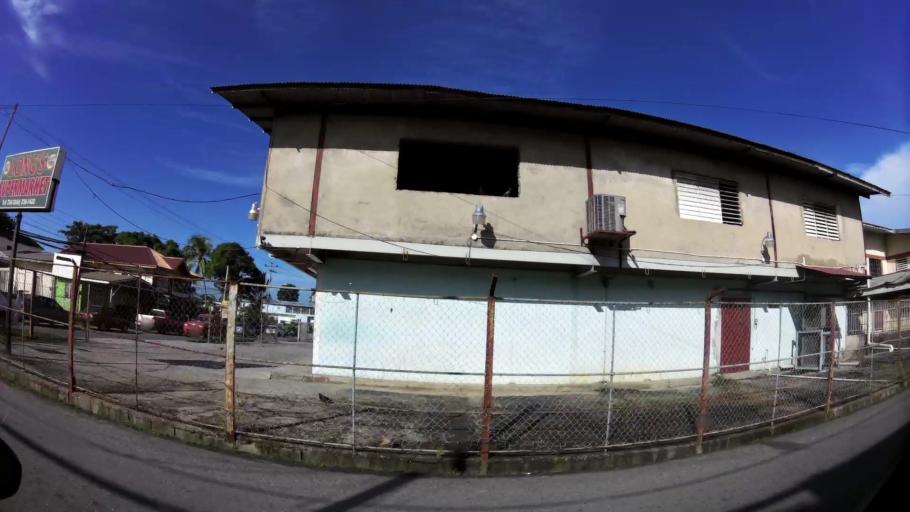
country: TT
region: Chaguanas
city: Chaguanas
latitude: 10.5137
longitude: -61.3870
